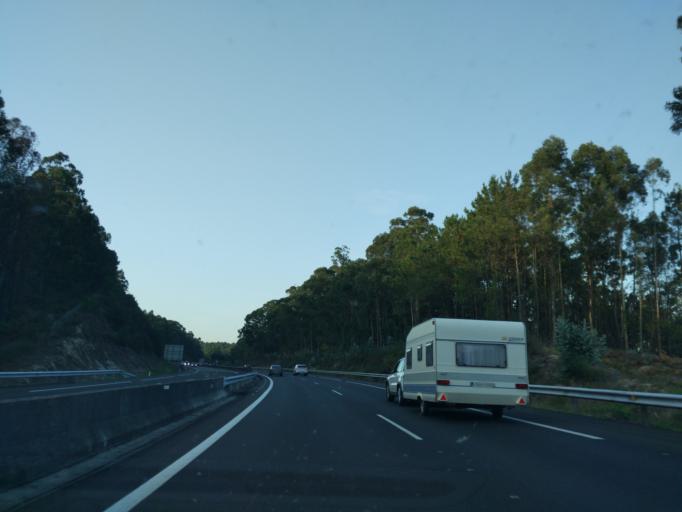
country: ES
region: Galicia
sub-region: Provincia de Pontevedra
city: Portas
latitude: 42.6020
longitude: -8.6698
